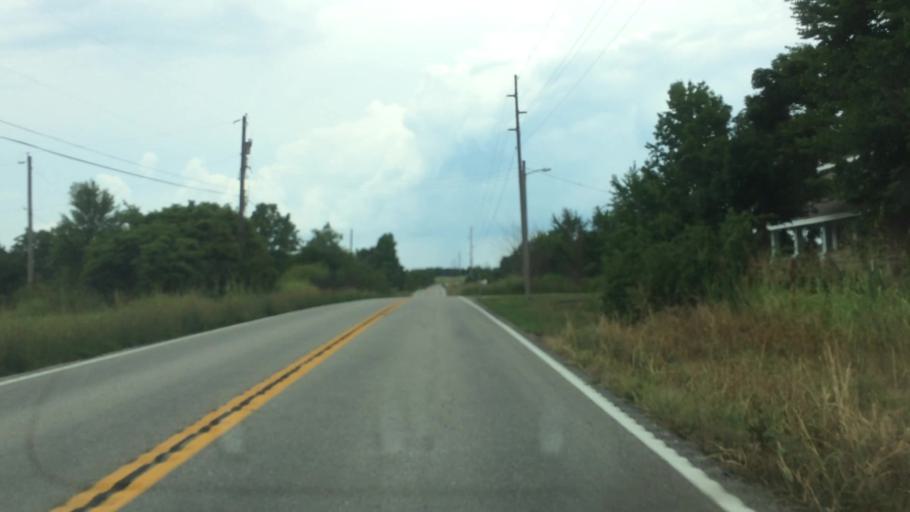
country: US
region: Missouri
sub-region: Greene County
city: Strafford
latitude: 37.2393
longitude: -93.1362
